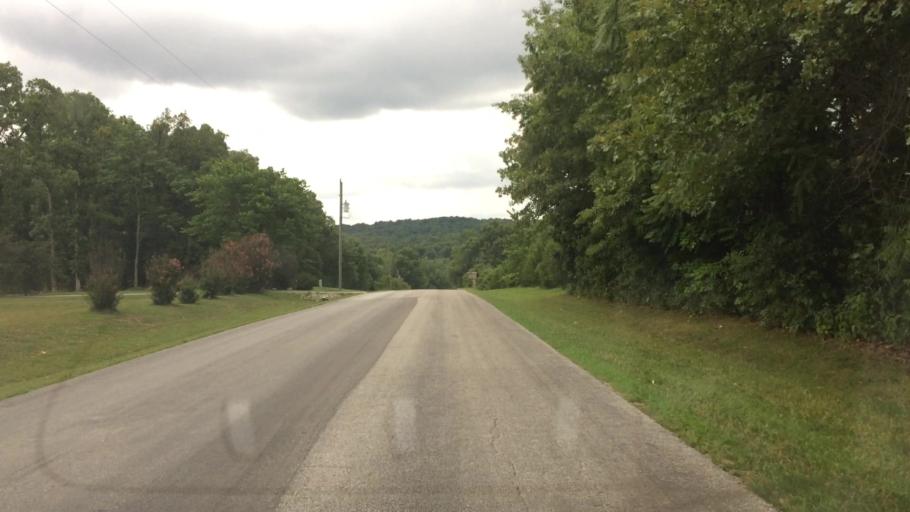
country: US
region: Missouri
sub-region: Webster County
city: Marshfield
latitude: 37.3082
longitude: -92.9846
